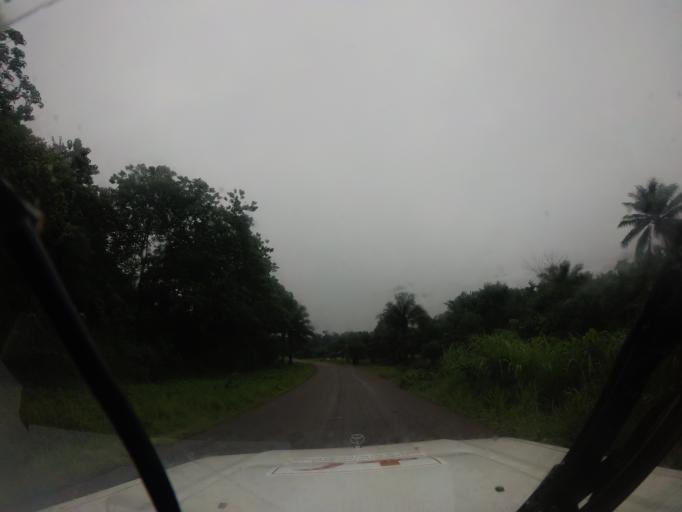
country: SL
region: Northern Province
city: Bumbuna
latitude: 9.3660
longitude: -11.8021
